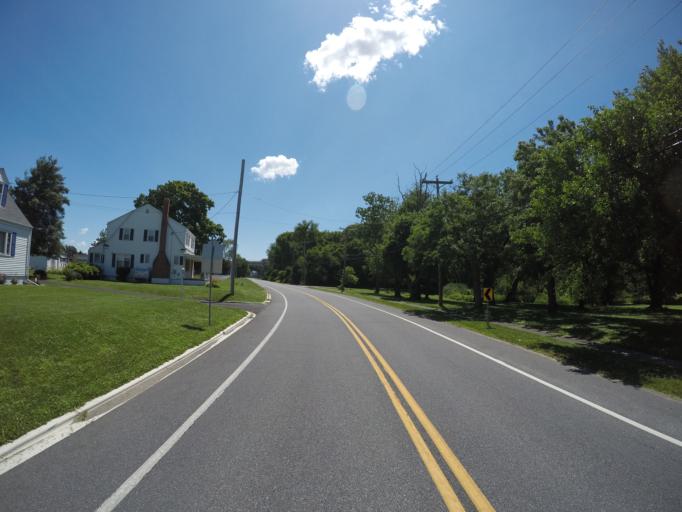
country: US
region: Delaware
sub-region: New Castle County
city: Delaware City
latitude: 39.5574
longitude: -75.6560
